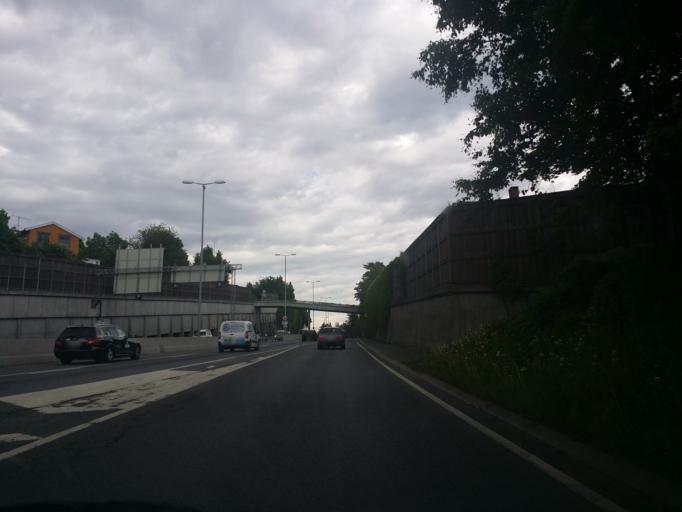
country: NO
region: Oslo
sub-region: Oslo
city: Sjolyststranda
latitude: 59.9394
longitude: 10.6895
